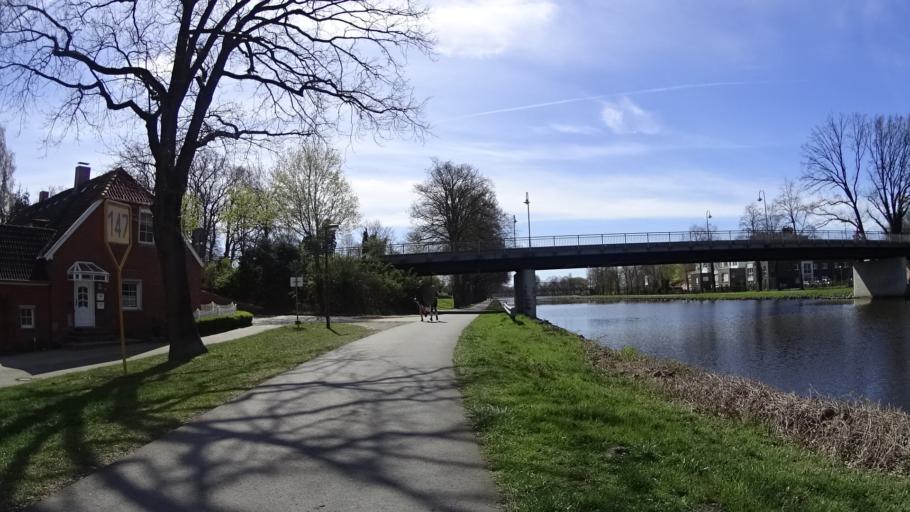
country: DE
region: Lower Saxony
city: Lingen
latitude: 52.5273
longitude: 7.3080
